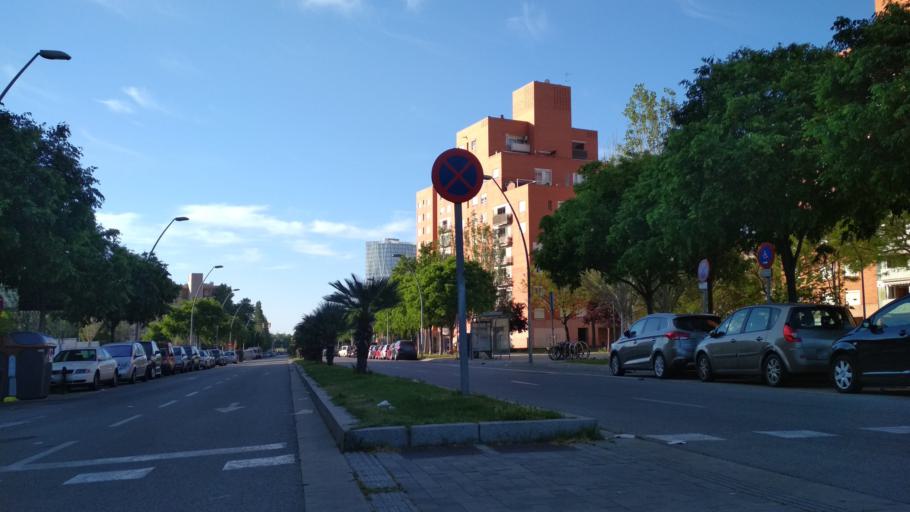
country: ES
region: Catalonia
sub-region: Provincia de Barcelona
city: Sant Adria de Besos
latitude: 41.4189
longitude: 2.2171
